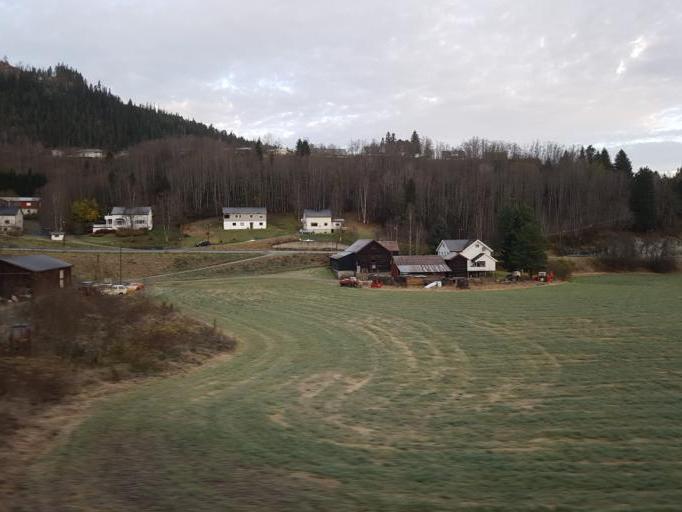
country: NO
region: Sor-Trondelag
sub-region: Midtre Gauldal
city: Storen
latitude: 63.0330
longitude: 10.2794
